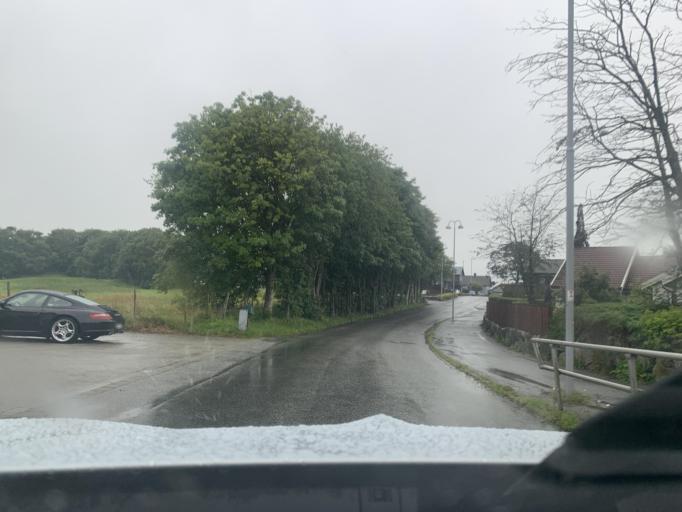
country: NO
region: Rogaland
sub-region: Time
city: Bryne
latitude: 58.7324
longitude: 5.6408
